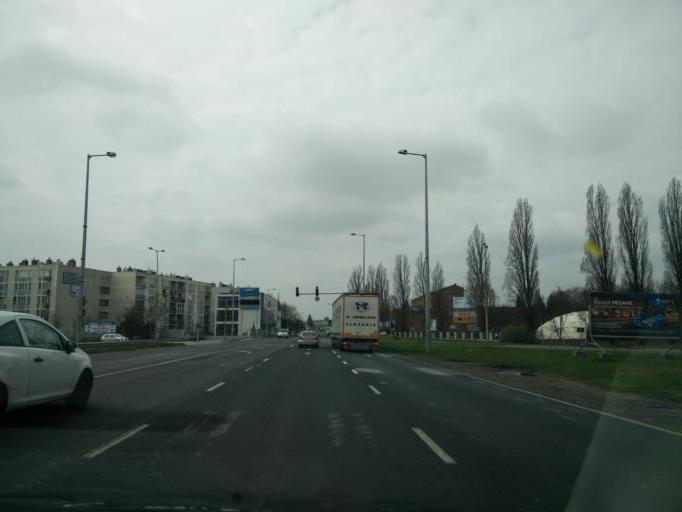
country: HU
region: Gyor-Moson-Sopron
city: Gyor
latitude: 47.6961
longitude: 17.6606
